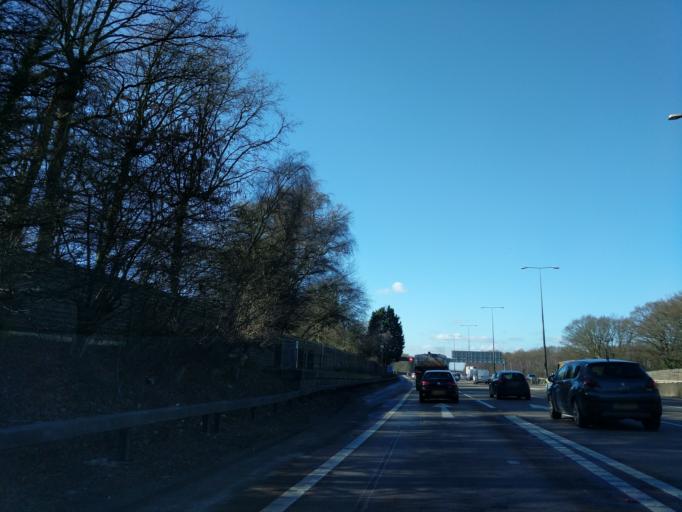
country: GB
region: England
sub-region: Surrey
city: Byfleet
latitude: 51.3243
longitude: -0.4606
